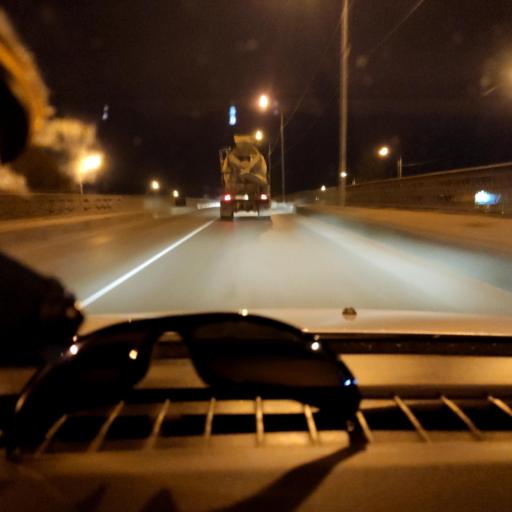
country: RU
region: Samara
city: Novokuybyshevsk
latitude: 53.1173
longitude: 50.0598
